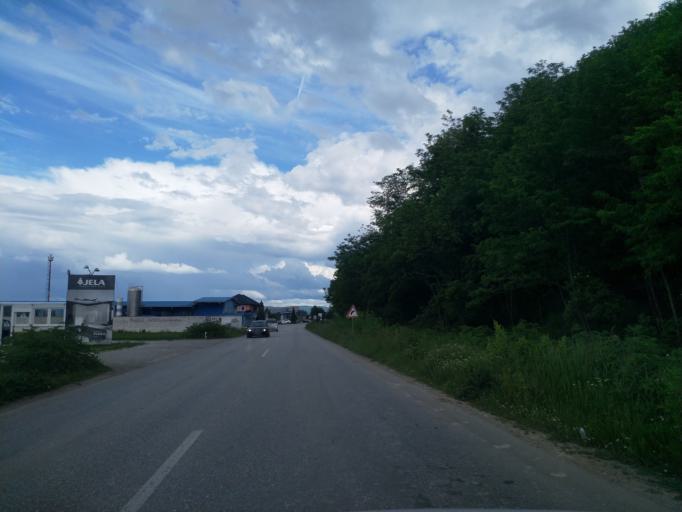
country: RS
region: Central Serbia
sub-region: Pomoravski Okrug
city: Jagodina
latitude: 43.9541
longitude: 21.3133
